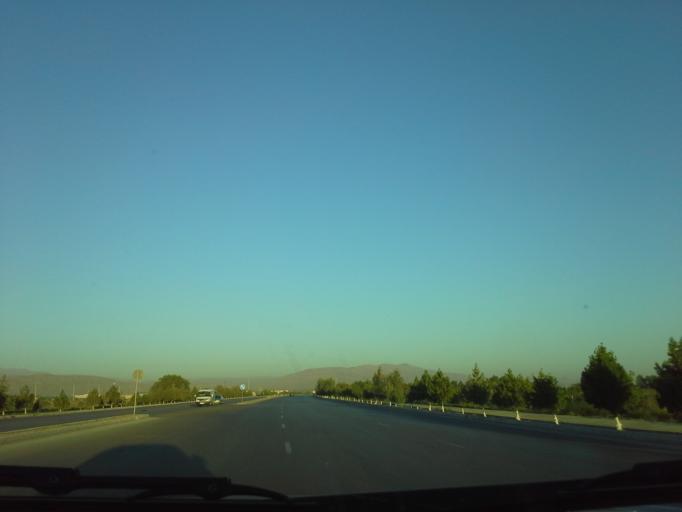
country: TM
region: Ahal
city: Abadan
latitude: 38.1038
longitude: 58.1388
